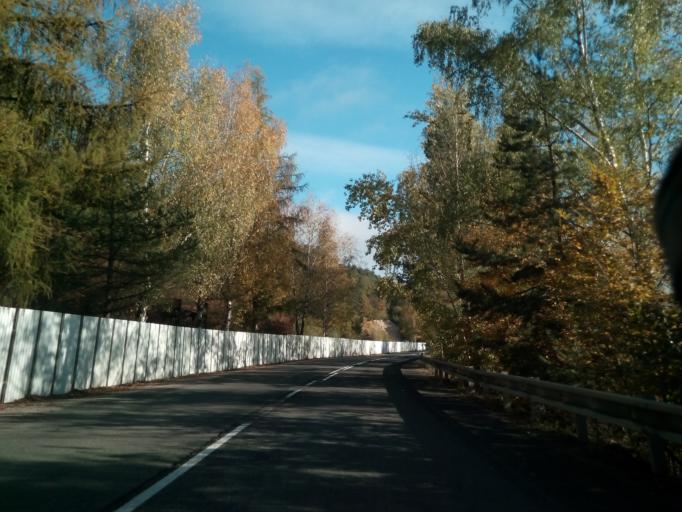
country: SK
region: Kosicky
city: Gelnica
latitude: 48.8837
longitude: 21.0011
